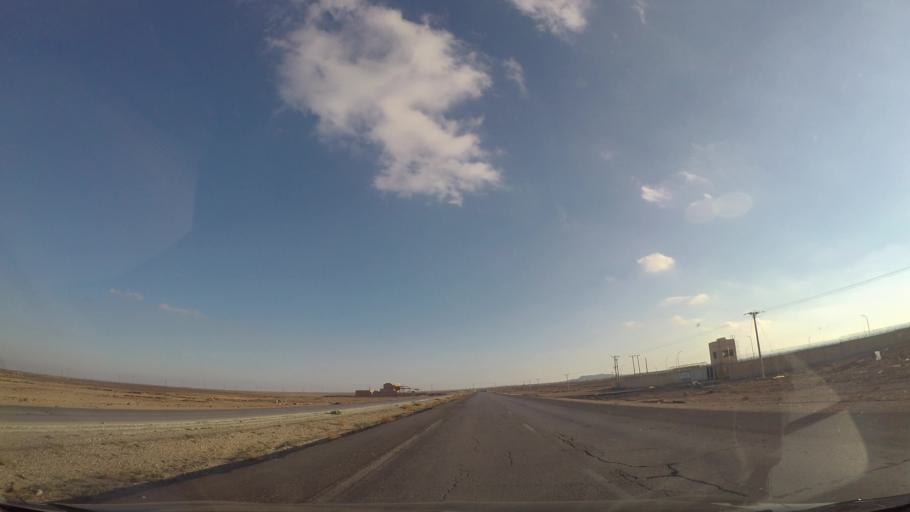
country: JO
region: Tafielah
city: Busayra
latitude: 30.5556
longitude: 35.7989
